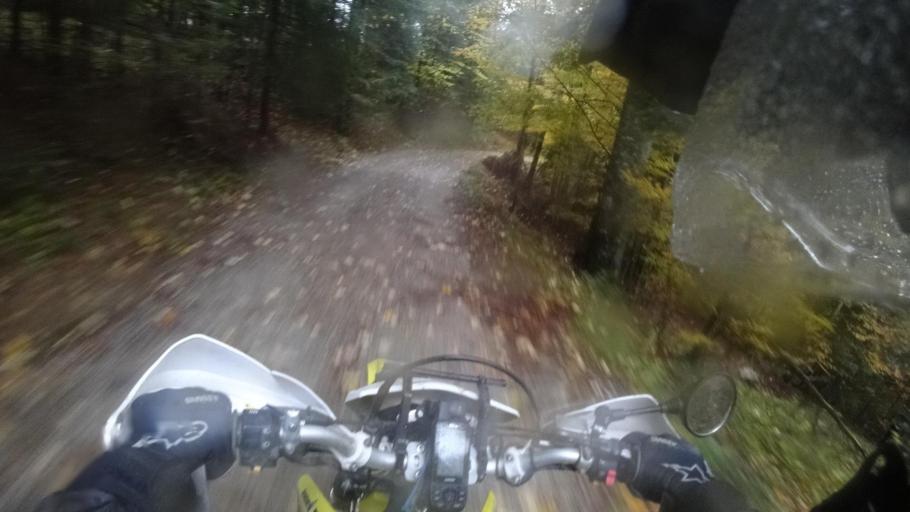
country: HR
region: Primorsko-Goranska
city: Vrbovsko
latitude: 45.3016
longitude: 14.9629
